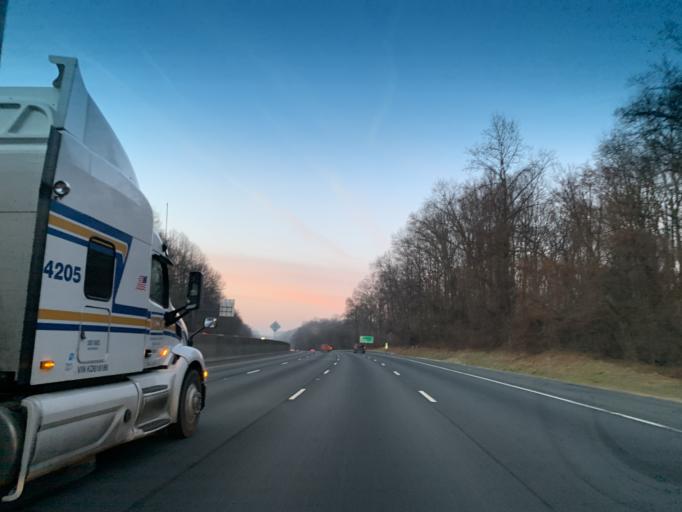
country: US
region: Maryland
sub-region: Harford County
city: Joppatowne
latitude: 39.4408
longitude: -76.3711
